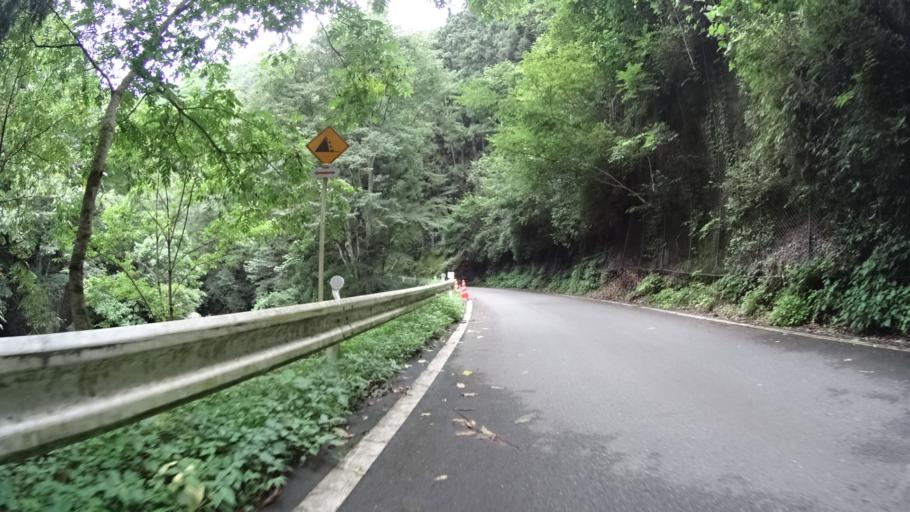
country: JP
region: Nagano
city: Saku
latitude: 36.0675
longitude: 138.6848
